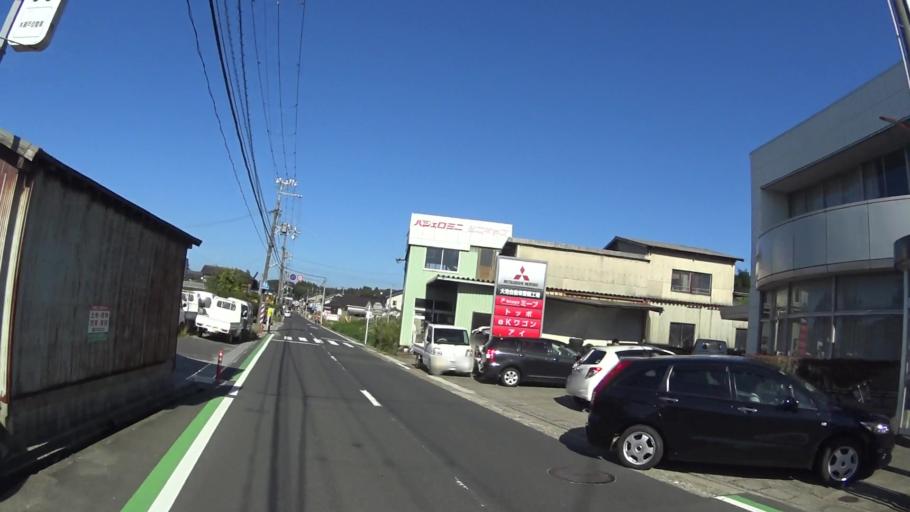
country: JP
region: Hyogo
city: Toyooka
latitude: 35.6292
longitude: 134.9267
